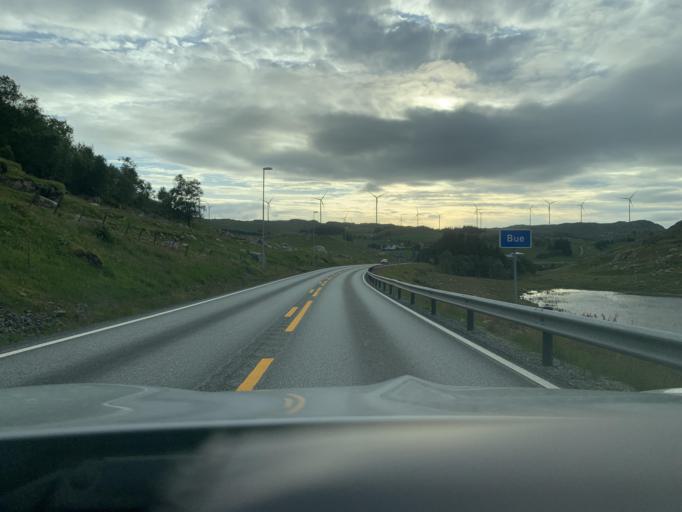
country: NO
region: Rogaland
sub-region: Bjerkreim
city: Vikesa
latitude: 58.6640
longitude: 5.9984
